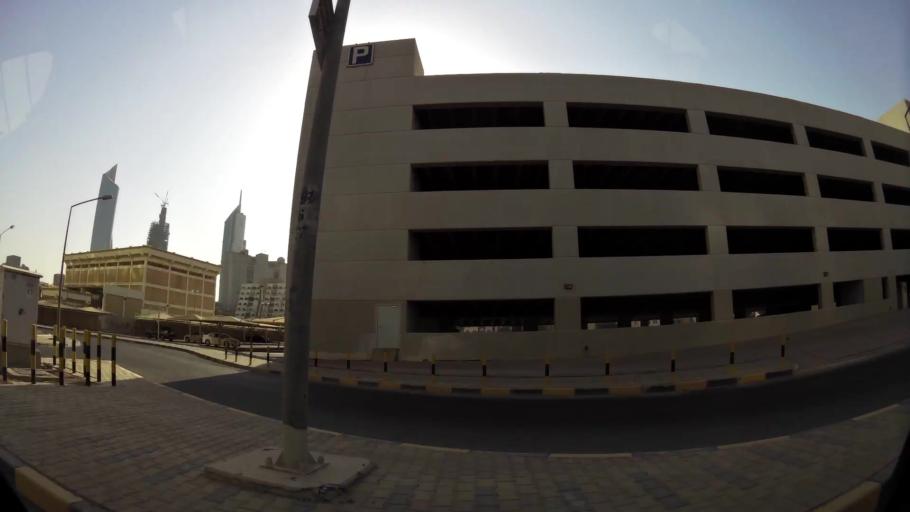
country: KW
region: Al Asimah
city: Kuwait City
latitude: 29.3779
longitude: 47.9809
